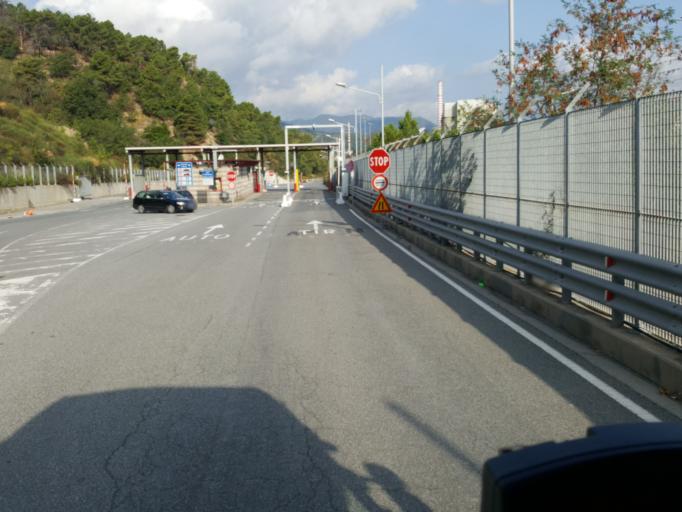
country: IT
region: Liguria
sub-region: Provincia di Savona
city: Vado Ligure
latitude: 44.2615
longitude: 8.4441
